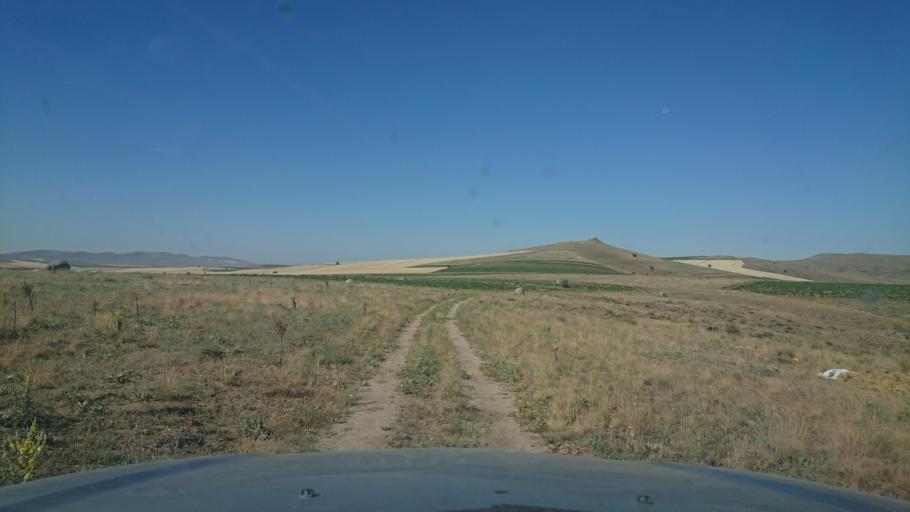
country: TR
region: Aksaray
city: Agacoren
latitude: 38.8385
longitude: 33.9409
